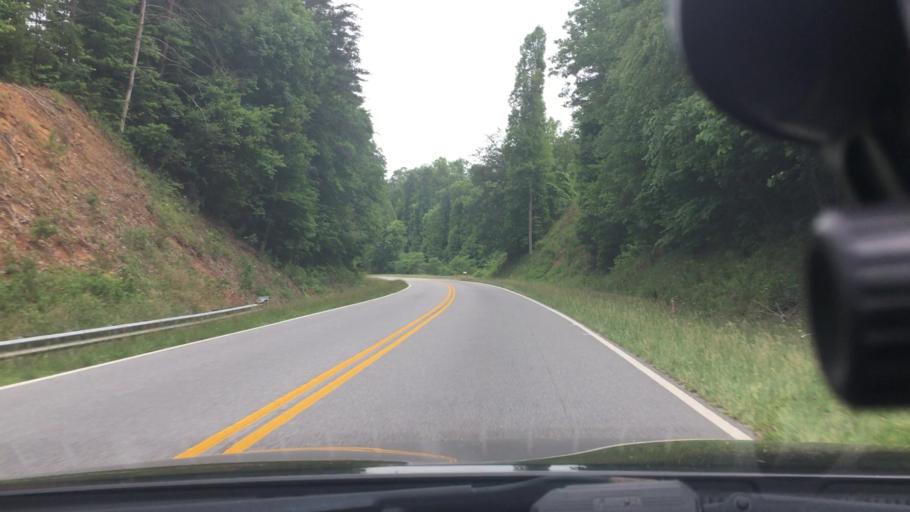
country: US
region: North Carolina
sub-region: McDowell County
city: West Marion
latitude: 35.5644
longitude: -81.9701
